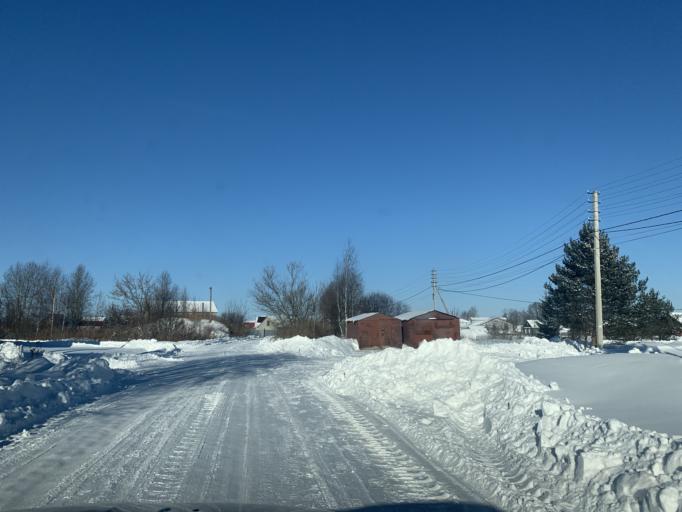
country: RU
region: Jaroslavl
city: Tunoshna
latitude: 57.6612
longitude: 40.0679
